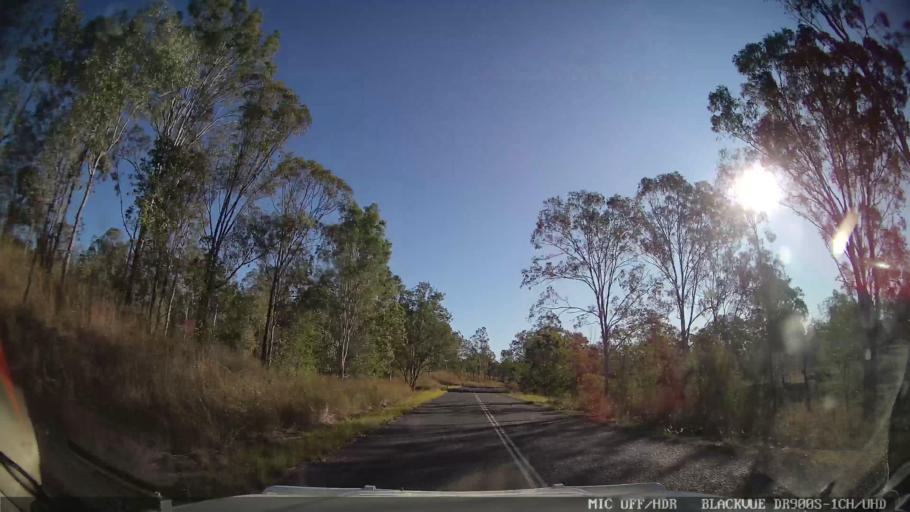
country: AU
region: Queensland
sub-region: Bundaberg
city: Sharon
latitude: -24.8053
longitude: 151.6561
